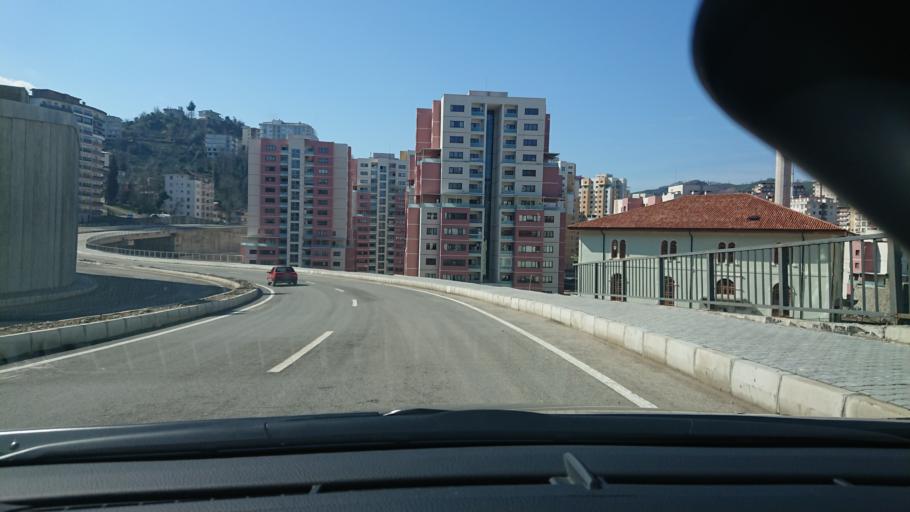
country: TR
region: Rize
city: Rize
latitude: 41.0173
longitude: 40.5178
